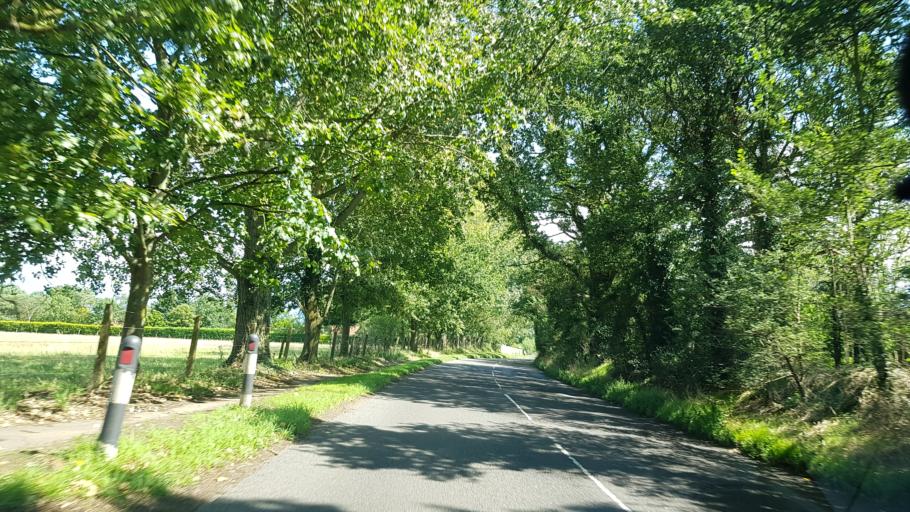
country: GB
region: England
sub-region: Surrey
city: Ripley
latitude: 51.3009
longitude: -0.5052
